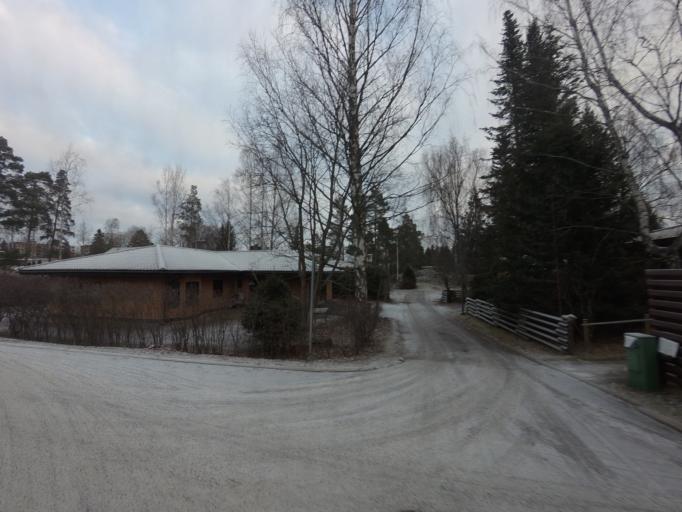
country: FI
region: Uusimaa
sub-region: Helsinki
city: Espoo
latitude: 60.2000
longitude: 24.6809
